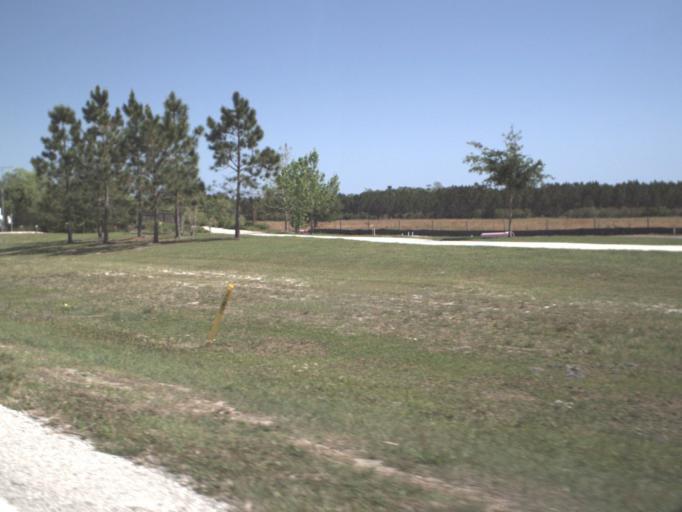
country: US
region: Florida
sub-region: Flagler County
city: Palm Coast
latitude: 29.5839
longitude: -81.2786
